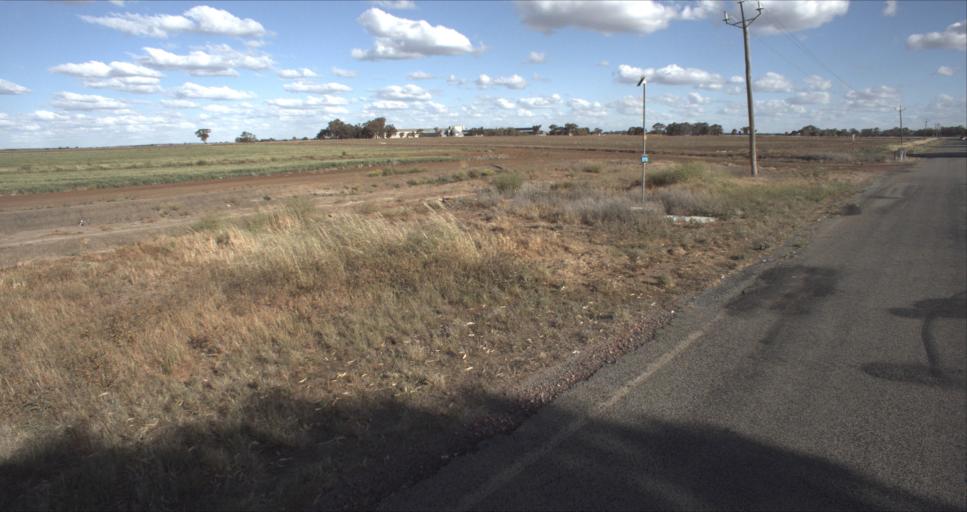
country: AU
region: New South Wales
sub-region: Leeton
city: Leeton
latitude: -34.5488
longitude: 146.2793
